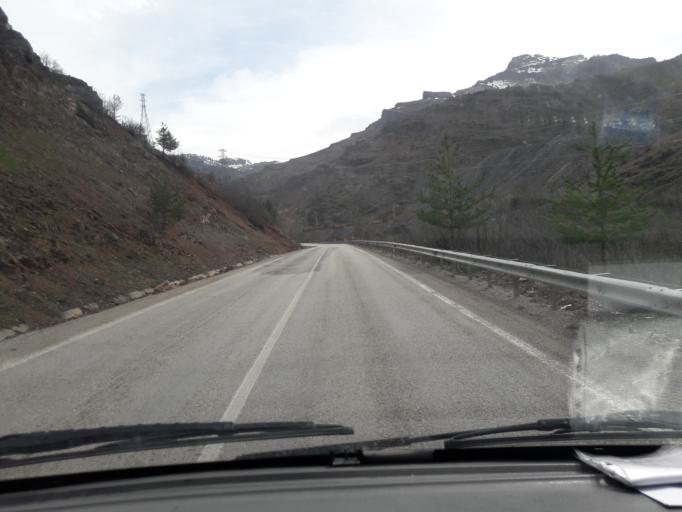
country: TR
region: Gumushane
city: Gumushkhane
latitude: 40.3044
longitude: 39.4765
